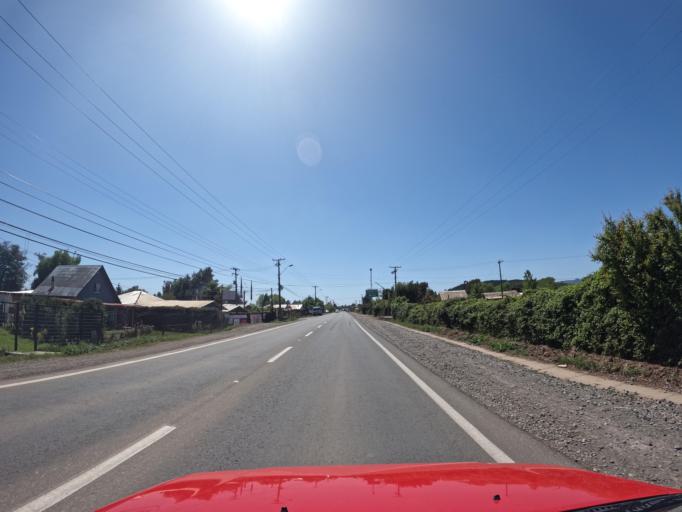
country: CL
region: Maule
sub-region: Provincia de Linares
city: Colbun
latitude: -35.7367
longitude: -71.4214
